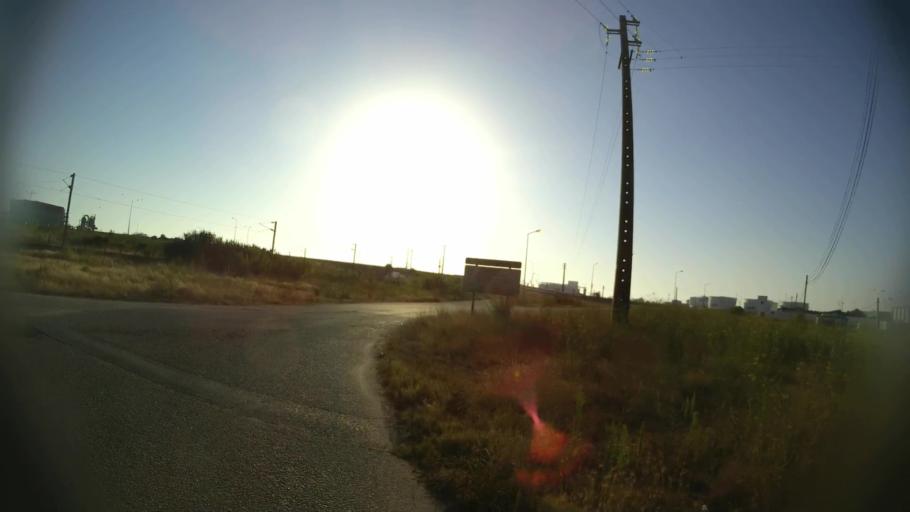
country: PT
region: Aveiro
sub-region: Ilhavo
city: Gafanha da Nazare
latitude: 40.6477
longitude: -8.7014
